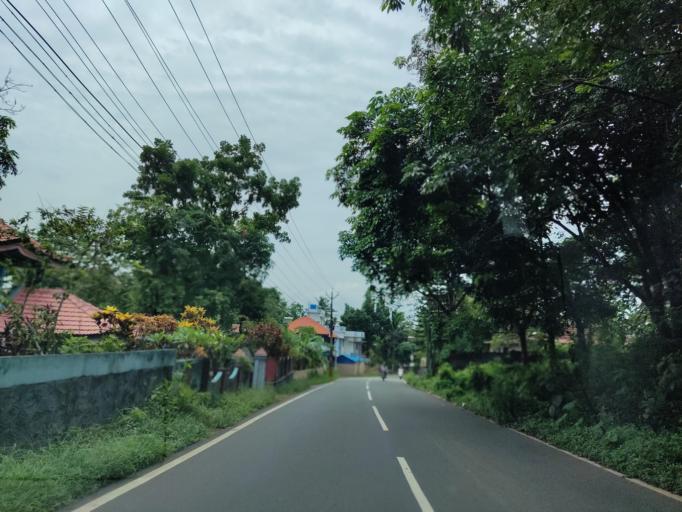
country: IN
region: Kerala
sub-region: Alappuzha
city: Chengannur
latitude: 9.2851
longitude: 76.6131
